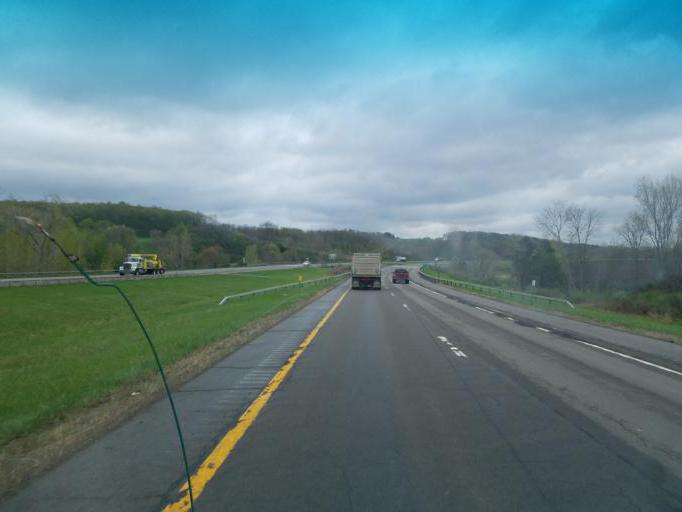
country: US
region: New York
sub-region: Chautauqua County
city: Falconer
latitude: 42.1346
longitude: -79.1825
